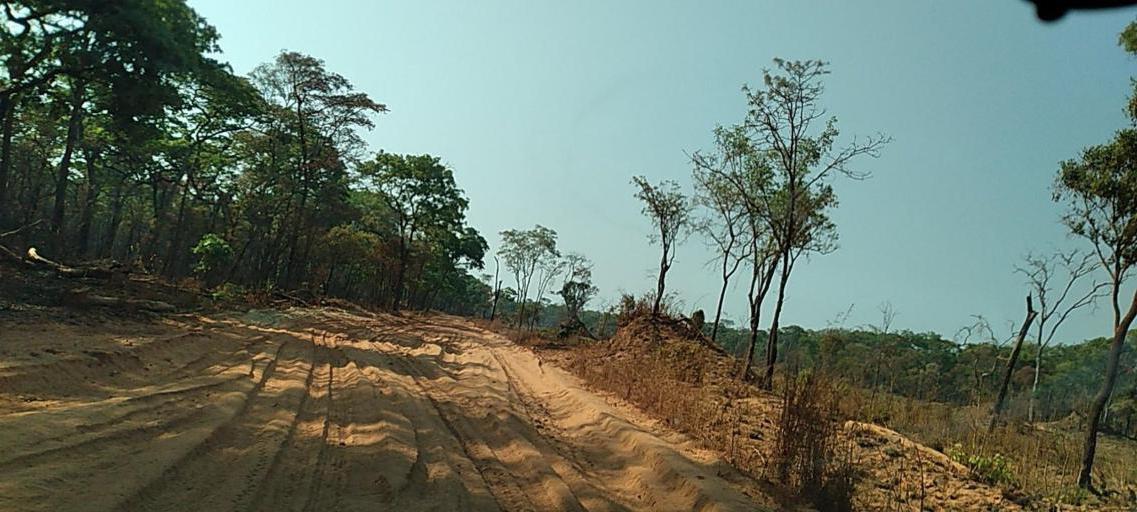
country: ZM
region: North-Western
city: Kasempa
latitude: -13.6365
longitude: 25.9930
